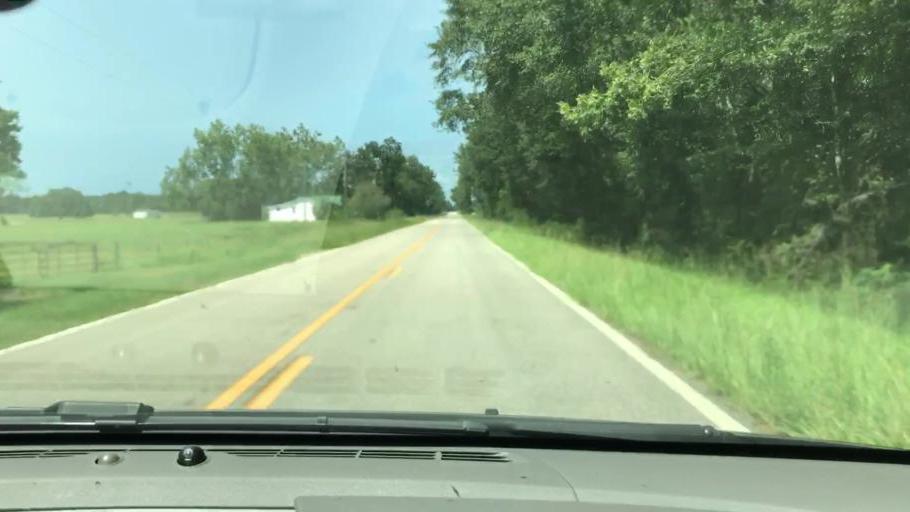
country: US
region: Georgia
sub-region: Seminole County
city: Donalsonville
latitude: 31.1341
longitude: -84.9952
